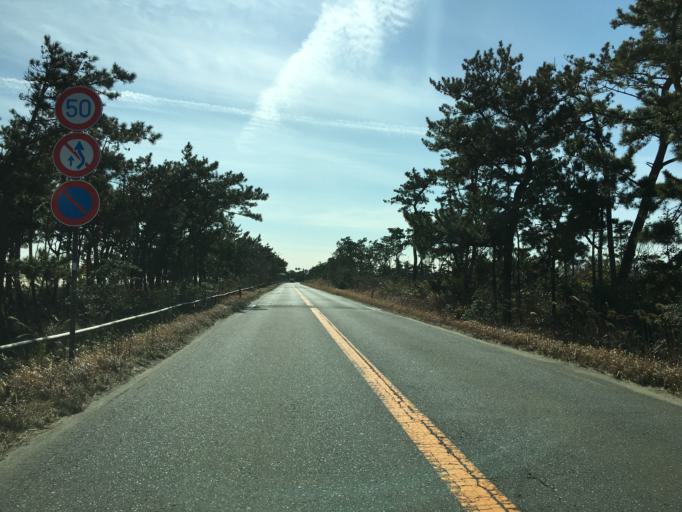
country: JP
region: Fukushima
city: Iwaki
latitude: 37.0701
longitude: 140.9767
